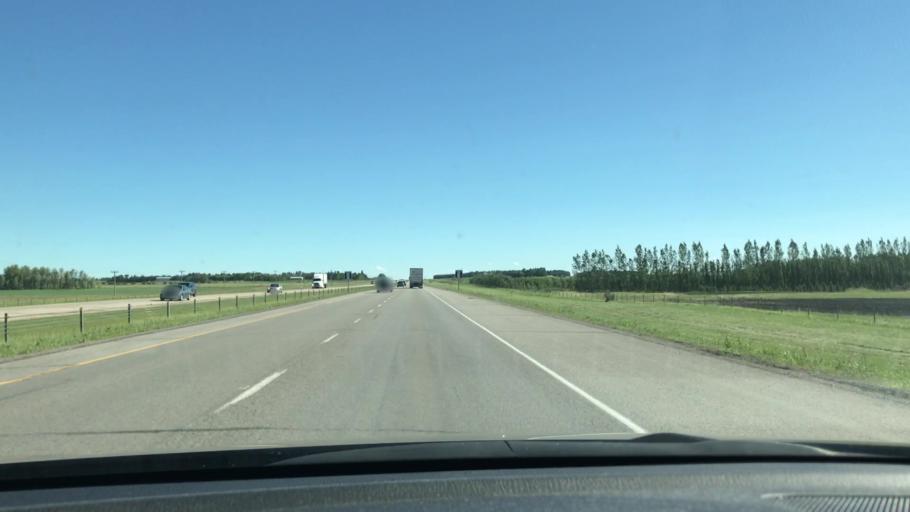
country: CA
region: Alberta
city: Olds
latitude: 51.9020
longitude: -114.0257
